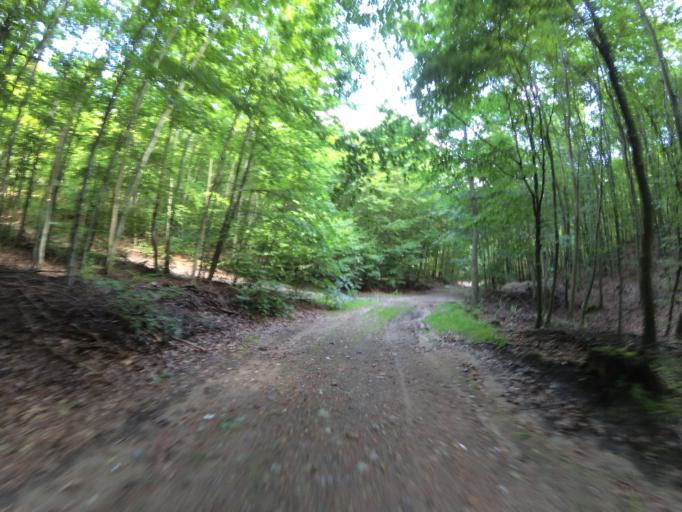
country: PL
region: Pomeranian Voivodeship
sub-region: Gdynia
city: Wielki Kack
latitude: 54.5124
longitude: 18.4527
